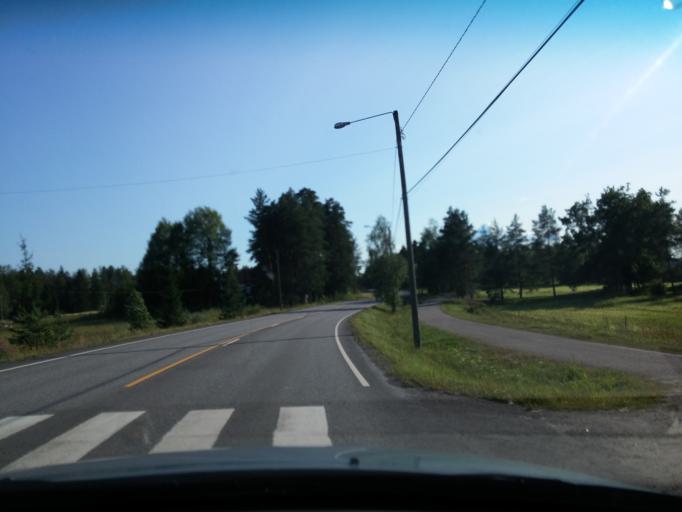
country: FI
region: Uusimaa
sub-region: Porvoo
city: Askola
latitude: 60.5025
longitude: 25.5629
